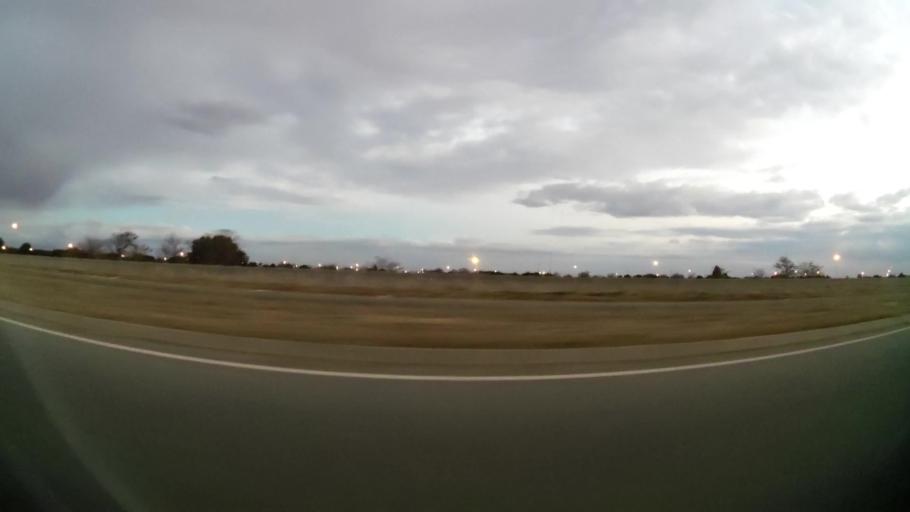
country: ZA
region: Orange Free State
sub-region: Lejweleputswa District Municipality
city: Welkom
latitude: -27.9501
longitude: 26.7947
